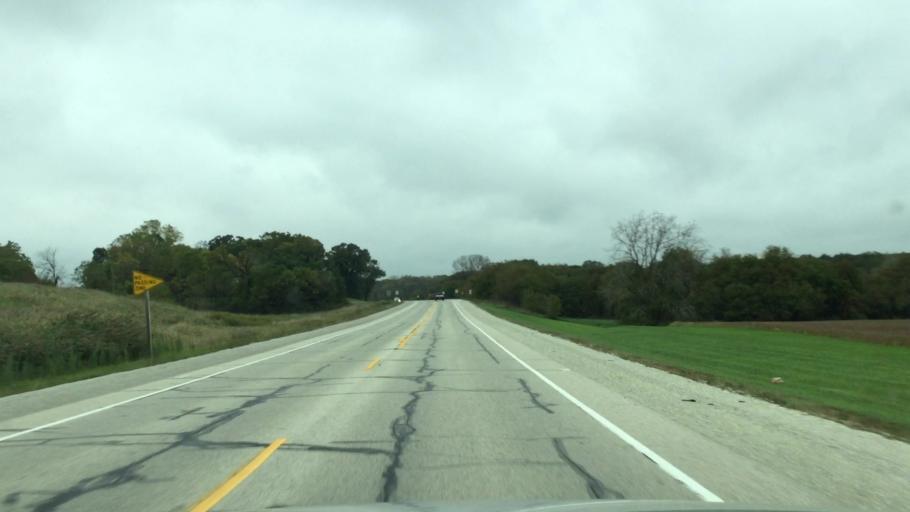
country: US
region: Wisconsin
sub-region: Racine County
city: Eagle Lake
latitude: 42.7423
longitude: -88.1421
